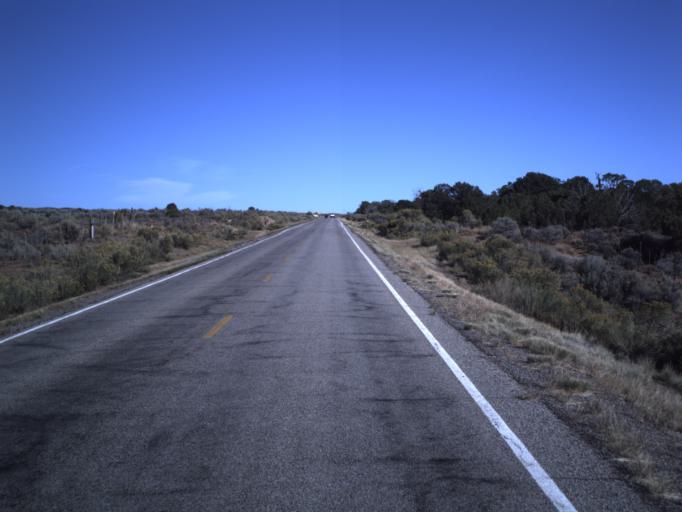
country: US
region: Utah
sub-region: Grand County
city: Moab
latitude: 38.3182
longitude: -109.3225
